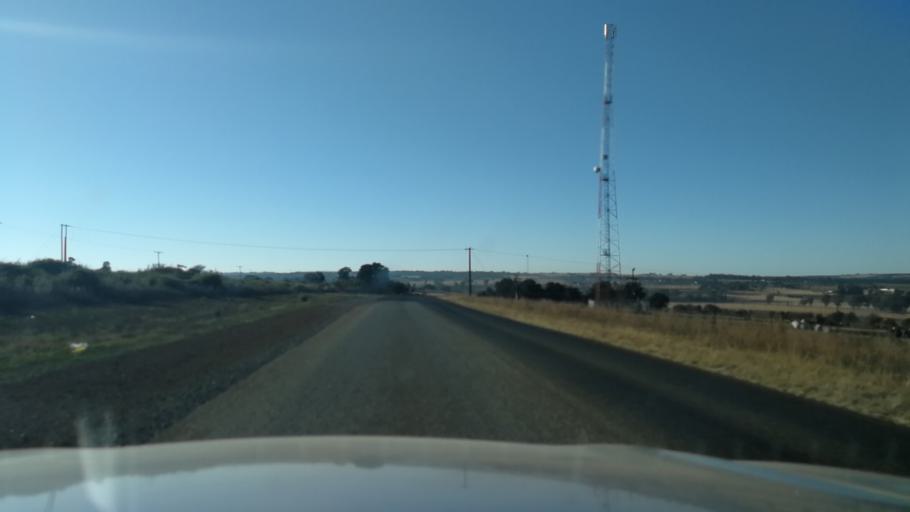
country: ZA
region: North-West
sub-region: Bojanala Platinum District Municipality
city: Rustenburg
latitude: -26.0001
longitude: 27.3090
